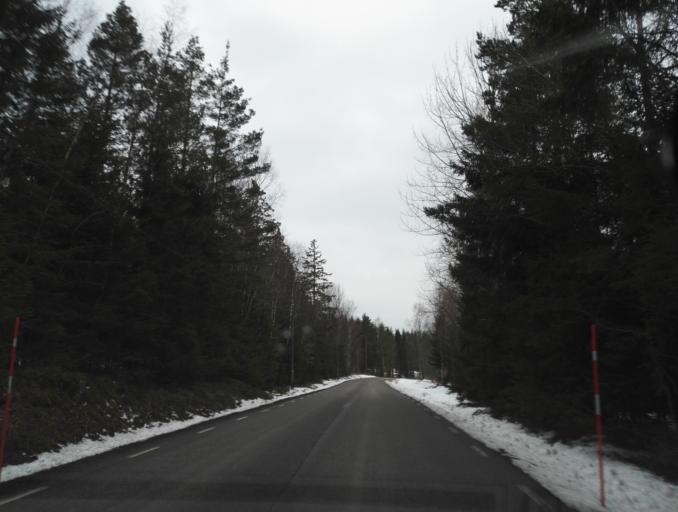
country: SE
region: Vaestra Goetaland
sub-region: Harryda Kommun
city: Hindas
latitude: 57.7294
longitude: 12.4886
